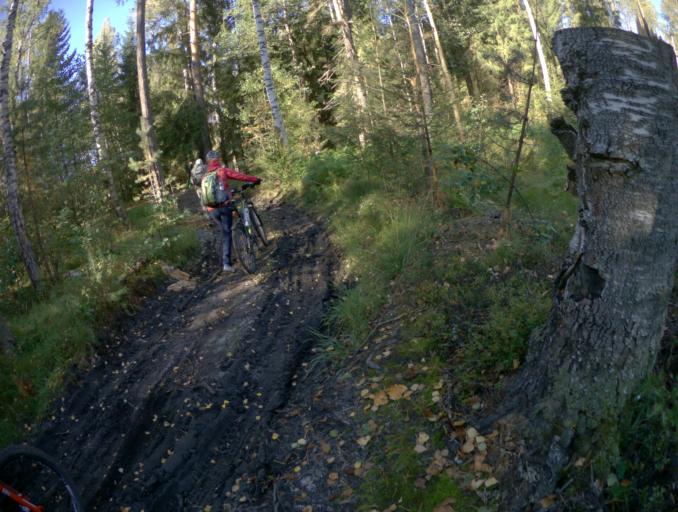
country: RU
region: Vladimir
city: Sobinka
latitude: 55.9611
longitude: 40.0014
